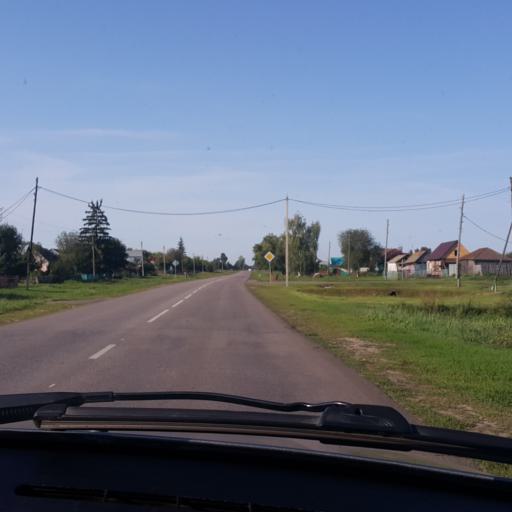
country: RU
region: Tambov
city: Novaya Lyada
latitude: 52.7835
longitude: 41.7640
